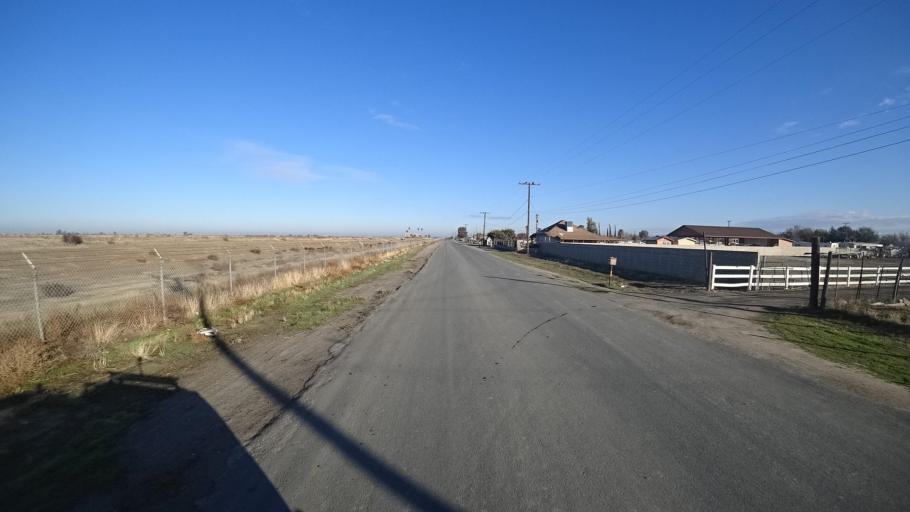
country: US
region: California
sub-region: Kern County
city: Delano
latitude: 35.7690
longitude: -119.2852
